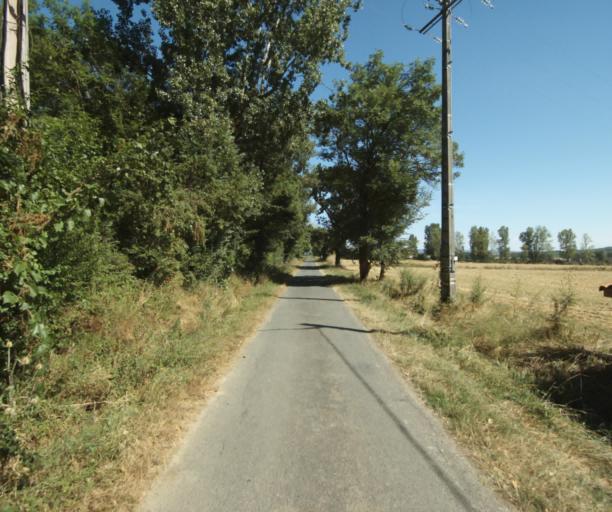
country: FR
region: Midi-Pyrenees
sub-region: Departement de la Haute-Garonne
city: Auriac-sur-Vendinelle
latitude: 43.5205
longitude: 1.8915
